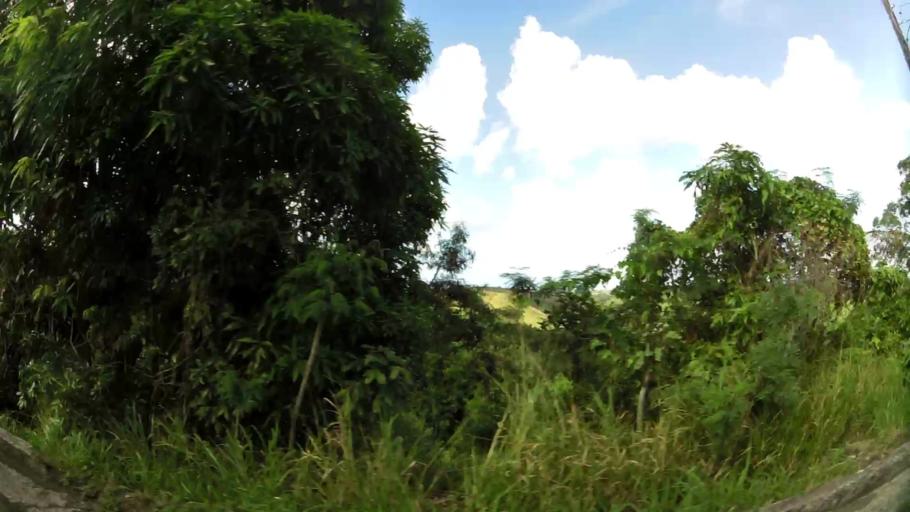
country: AG
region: Saint Peter
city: All Saints
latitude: 17.0443
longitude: -61.8180
